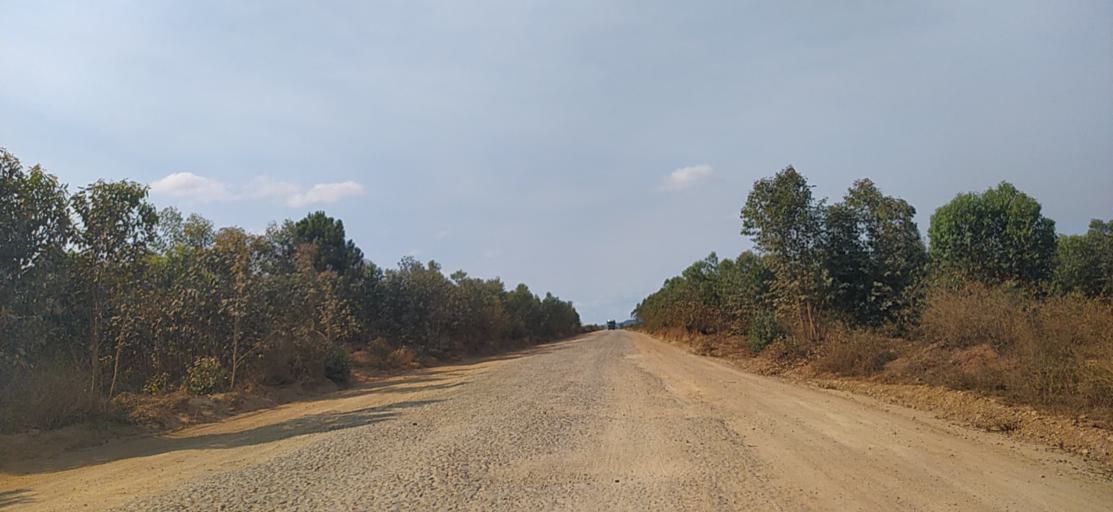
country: MG
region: Alaotra Mangoro
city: Moramanga
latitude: -18.6823
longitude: 48.2719
